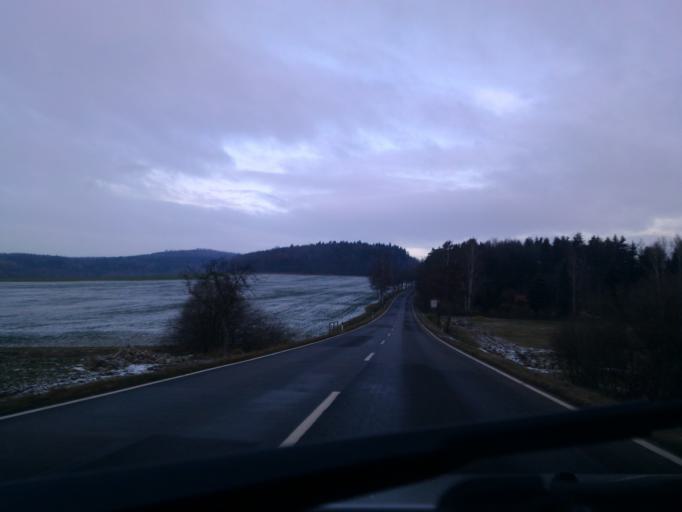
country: DE
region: Saxony
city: Grossschonau
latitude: 50.9101
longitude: 14.6615
